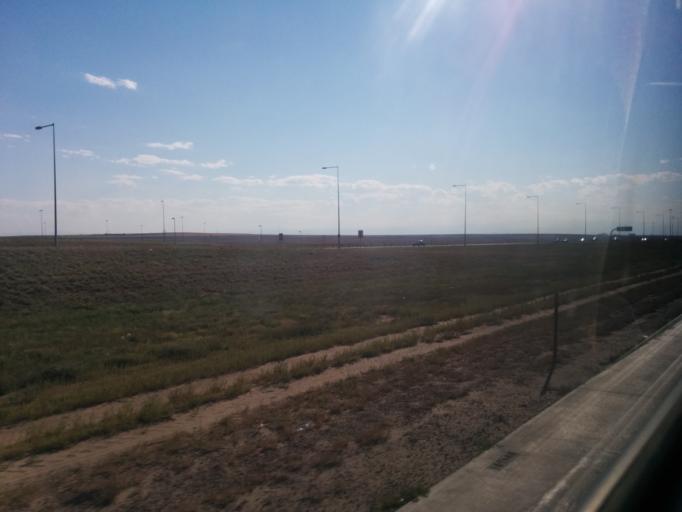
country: US
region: Colorado
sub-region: Adams County
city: Aurora
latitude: 39.8343
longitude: -104.7096
